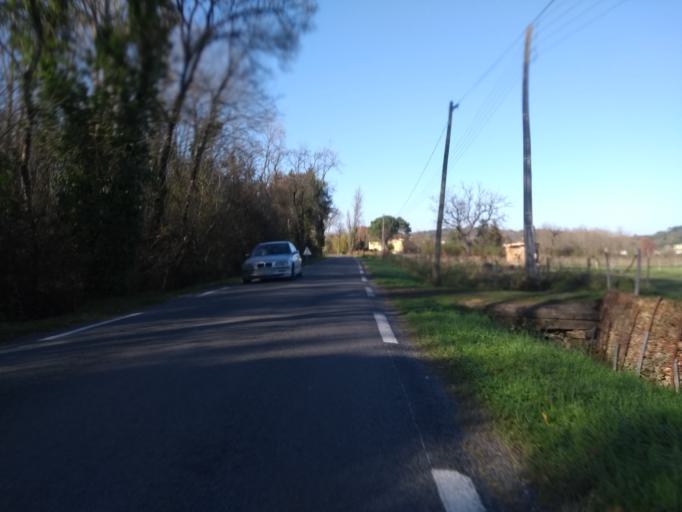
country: FR
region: Aquitaine
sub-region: Departement de la Gironde
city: Cambes
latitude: 44.7210
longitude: -0.4701
